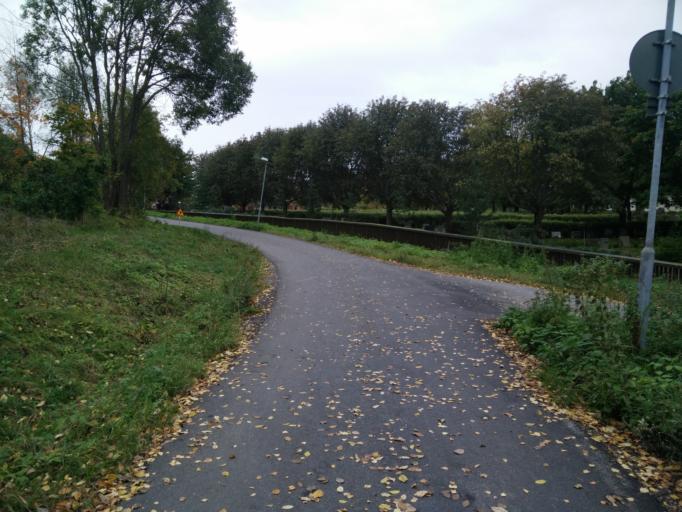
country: SE
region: Vaesternorrland
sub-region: Sundsvalls Kommun
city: Sundsvall
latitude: 62.3981
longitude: 17.2720
